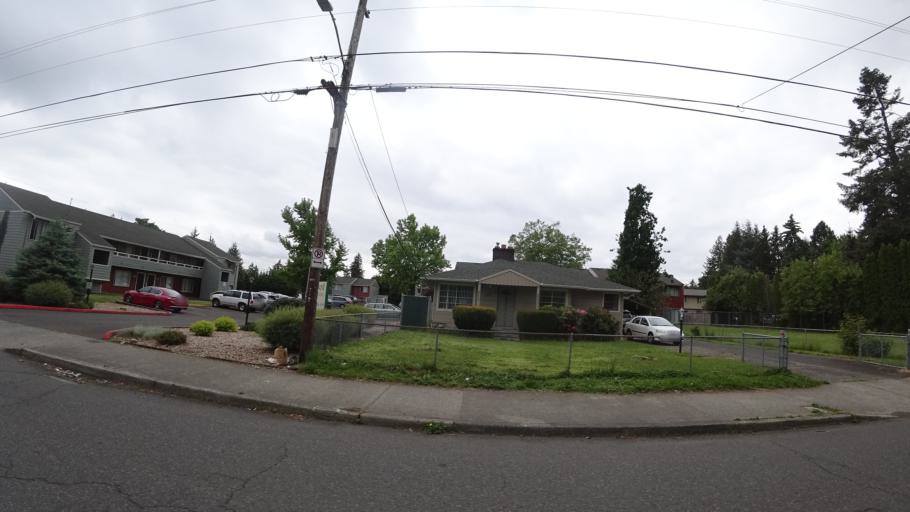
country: US
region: Oregon
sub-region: Multnomah County
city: Lents
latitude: 45.5050
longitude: -122.5248
